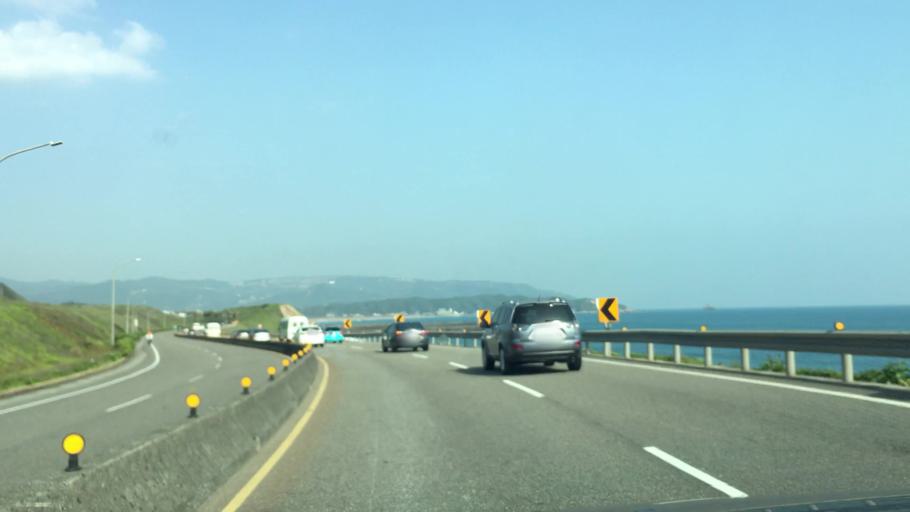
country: TW
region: Taiwan
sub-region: Keelung
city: Keelung
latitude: 25.2022
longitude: 121.6704
